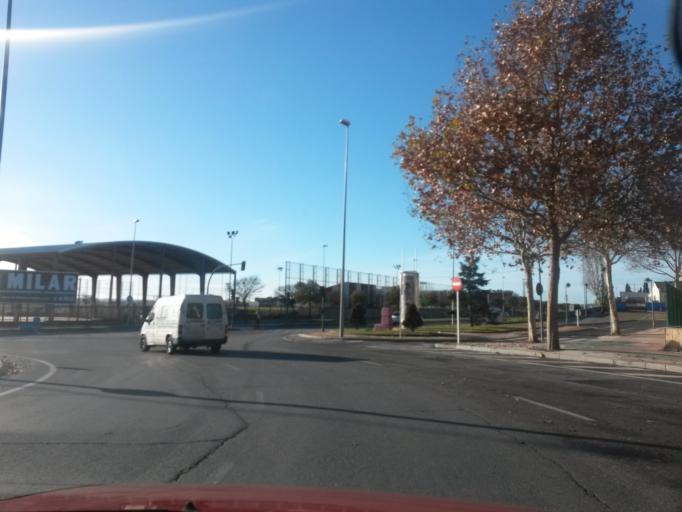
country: ES
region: Castille and Leon
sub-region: Provincia de Salamanca
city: Salamanca
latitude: 40.9722
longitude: -5.6811
